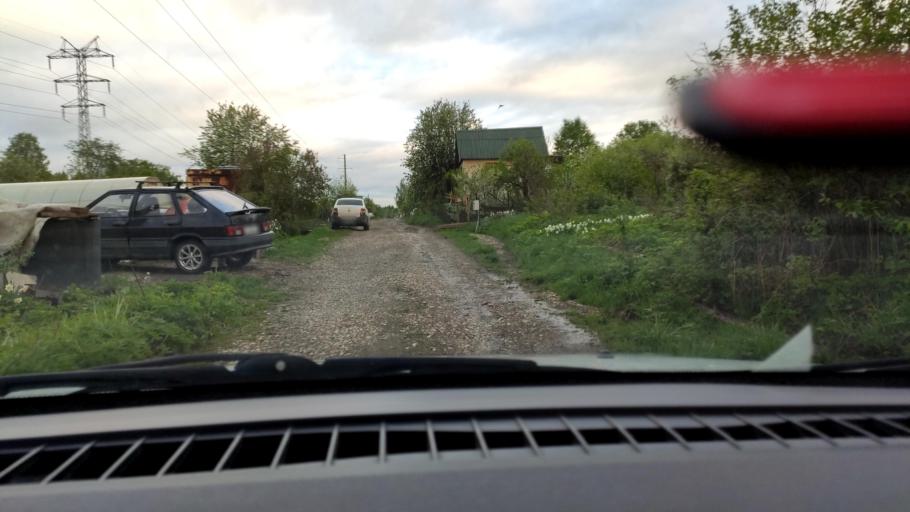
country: RU
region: Perm
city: Polazna
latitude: 58.1298
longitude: 56.4143
